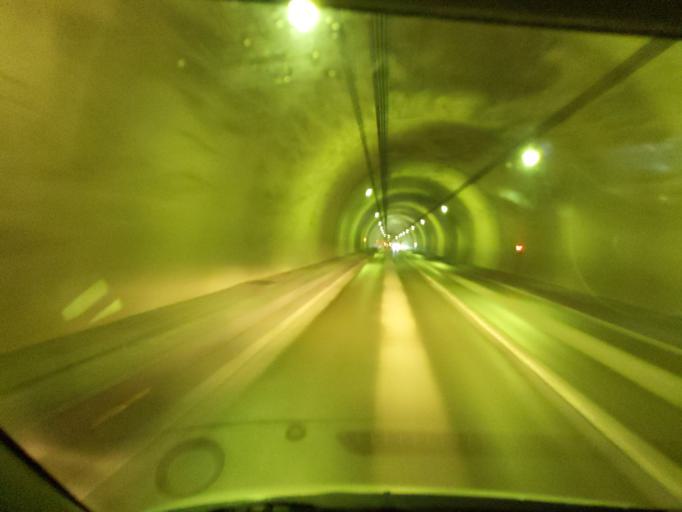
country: JP
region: Iwate
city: Tono
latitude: 39.1723
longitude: 141.3670
